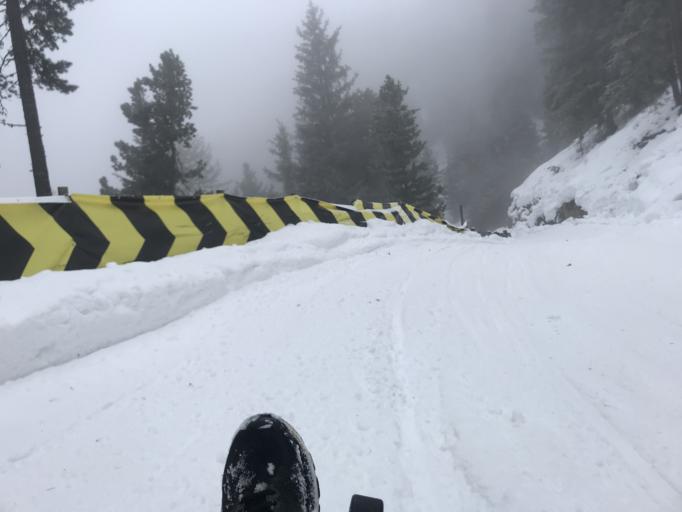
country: IT
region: Trentino-Alto Adige
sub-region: Bolzano
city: San Pietro
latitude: 46.6857
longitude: 11.7016
